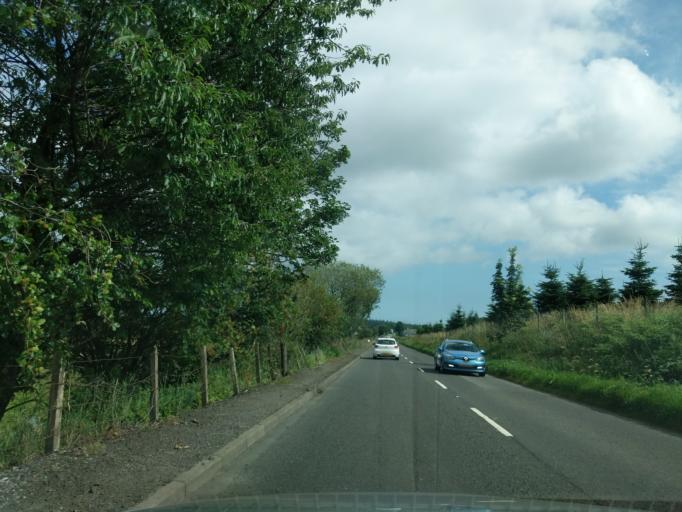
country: GB
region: Scotland
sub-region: Angus
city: Muirhead
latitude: 56.4989
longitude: -3.0812
